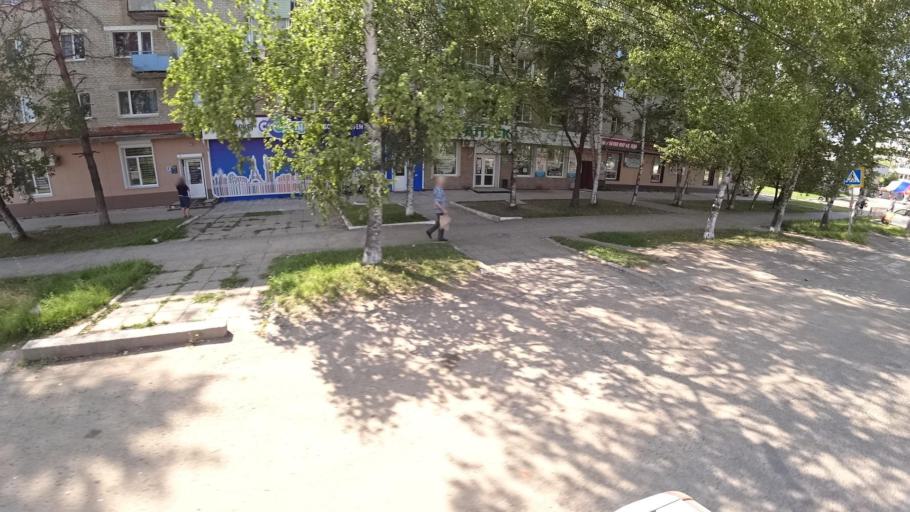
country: RU
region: Khabarovsk Krai
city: Khor
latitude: 47.9664
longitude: 135.0528
